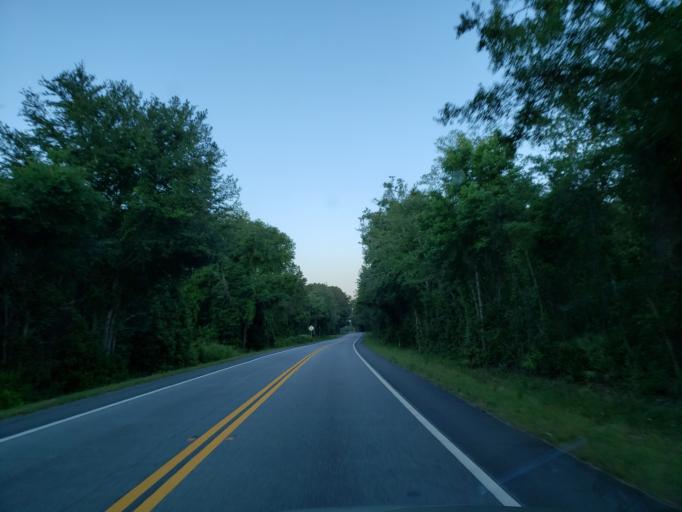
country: US
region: Florida
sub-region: Hamilton County
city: Jasper
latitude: 30.5558
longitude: -83.0801
